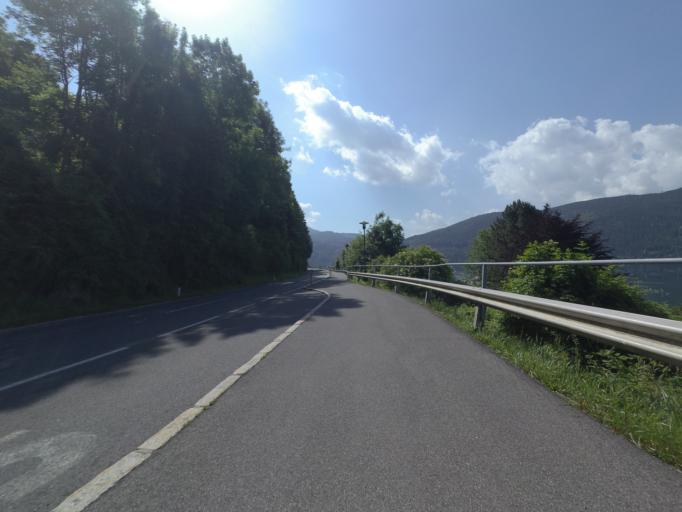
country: AT
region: Carinthia
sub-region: Politischer Bezirk Villach Land
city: Ferndorf
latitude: 46.7779
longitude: 13.6296
